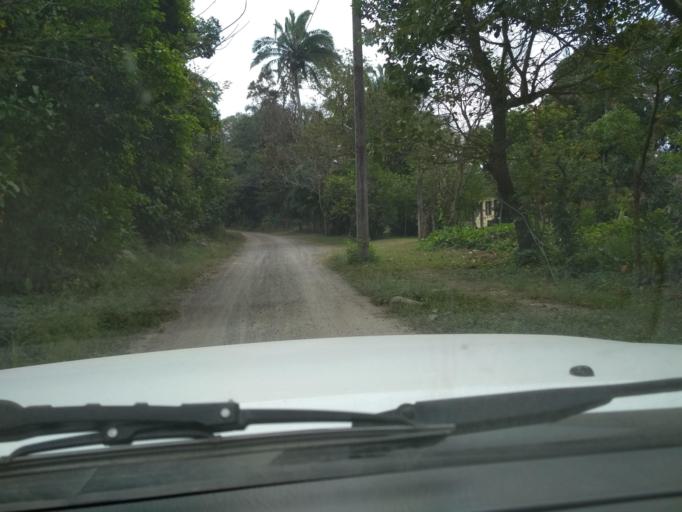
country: MX
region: Veracruz
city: El Tejar
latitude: 19.0747
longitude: -96.1709
